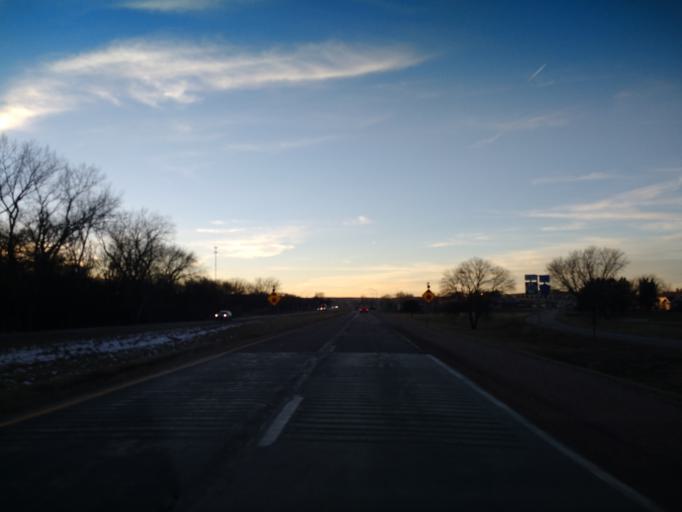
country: US
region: Iowa
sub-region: Woodbury County
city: Moville
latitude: 42.4820
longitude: -96.0720
